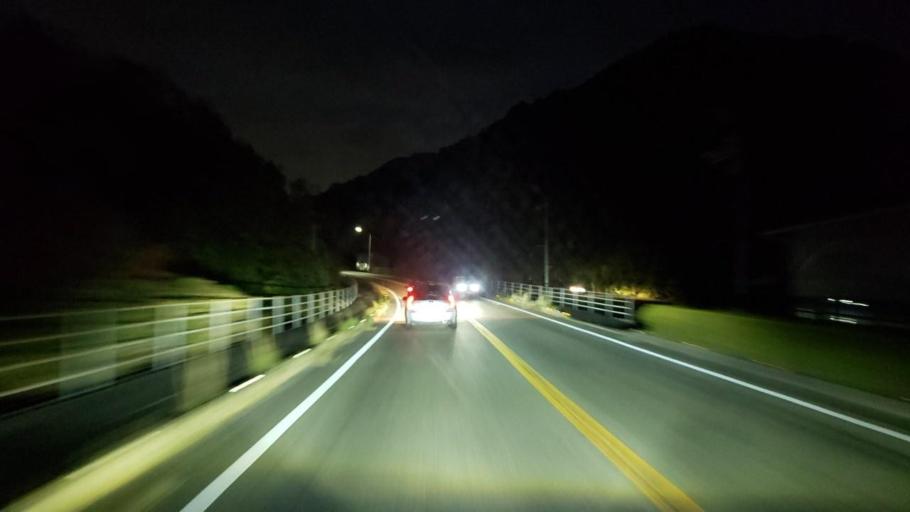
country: JP
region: Tokushima
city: Narutocho-mitsuishi
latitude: 34.2121
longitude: 134.5607
